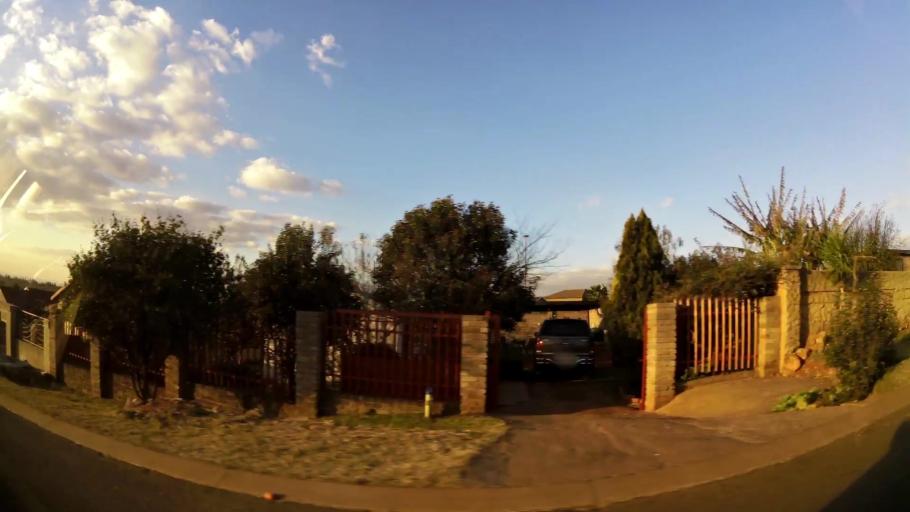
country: ZA
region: Gauteng
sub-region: West Rand District Municipality
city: Krugersdorp
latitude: -26.0727
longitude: 27.7544
